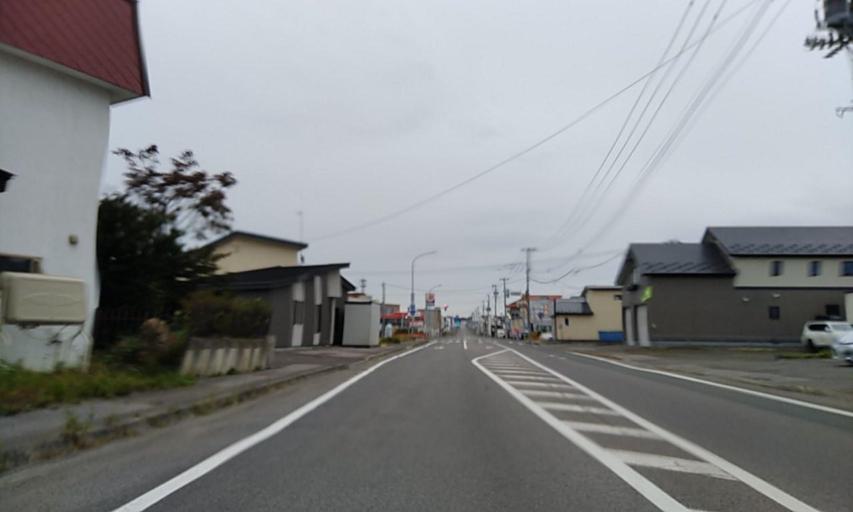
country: JP
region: Hokkaido
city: Bihoro
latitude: 43.8345
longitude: 144.1044
